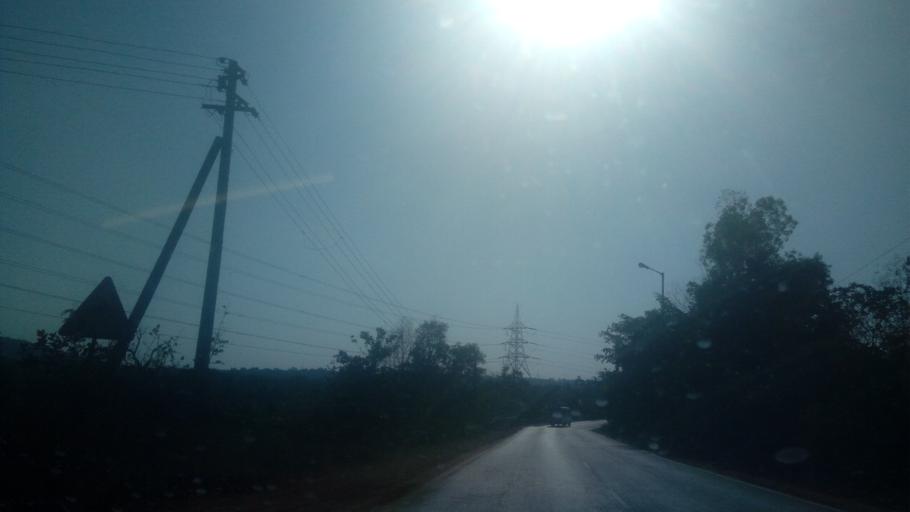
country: IN
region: Goa
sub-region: North Goa
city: Navelim
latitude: 15.5280
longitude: 73.9816
